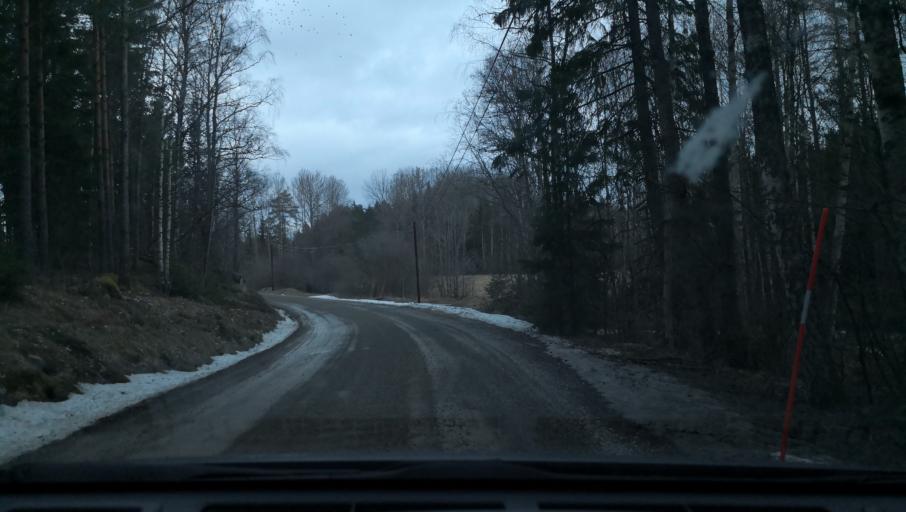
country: SE
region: Vaestmanland
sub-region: Kopings Kommun
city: Kolsva
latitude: 59.5805
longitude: 15.7140
